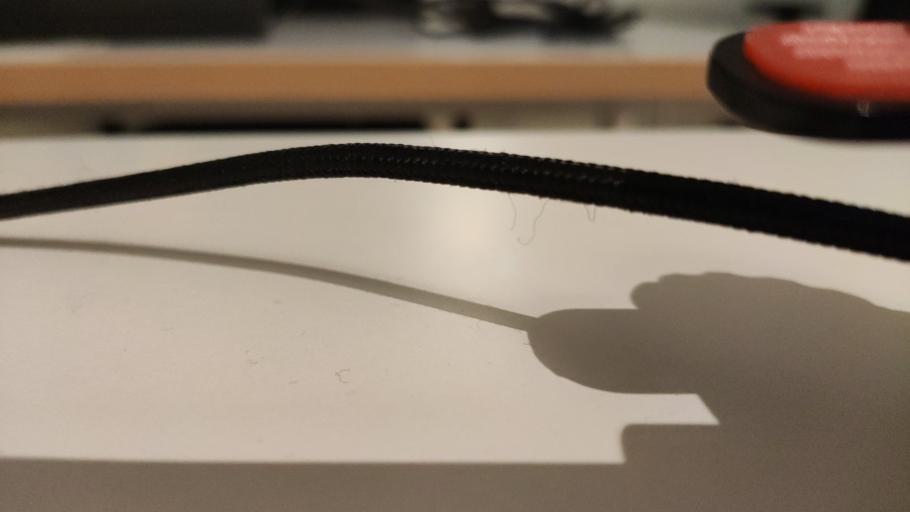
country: RU
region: Moskovskaya
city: Rogachevo
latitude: 56.4177
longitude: 37.2124
